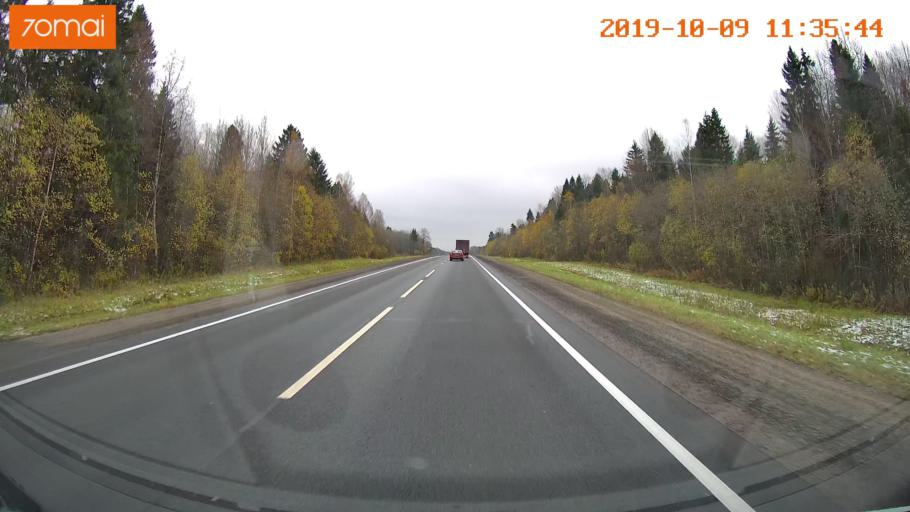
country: RU
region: Vologda
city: Gryazovets
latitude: 58.9995
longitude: 40.1293
